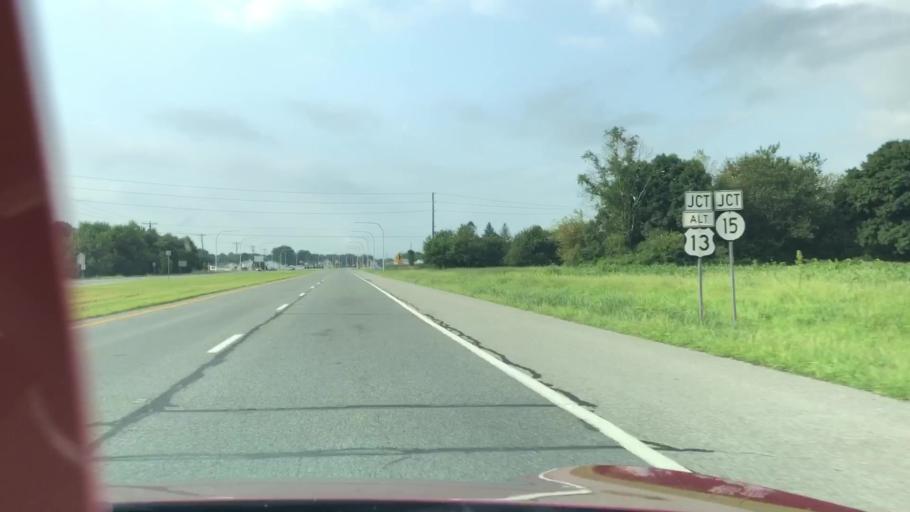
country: US
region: Delaware
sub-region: Kent County
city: Woodside East
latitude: 39.0503
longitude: -75.5569
